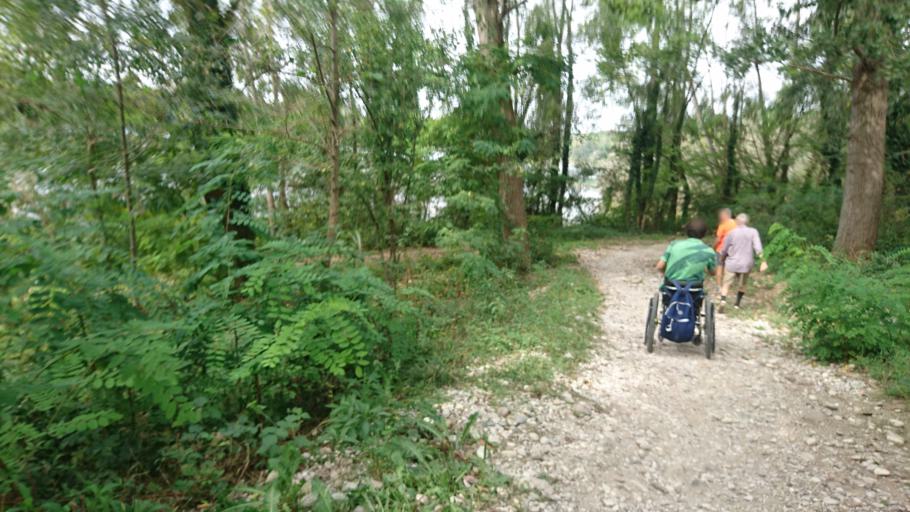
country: IT
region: Veneto
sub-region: Provincia di Padova
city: San Giorgio in Bosco
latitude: 45.5647
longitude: 11.7942
